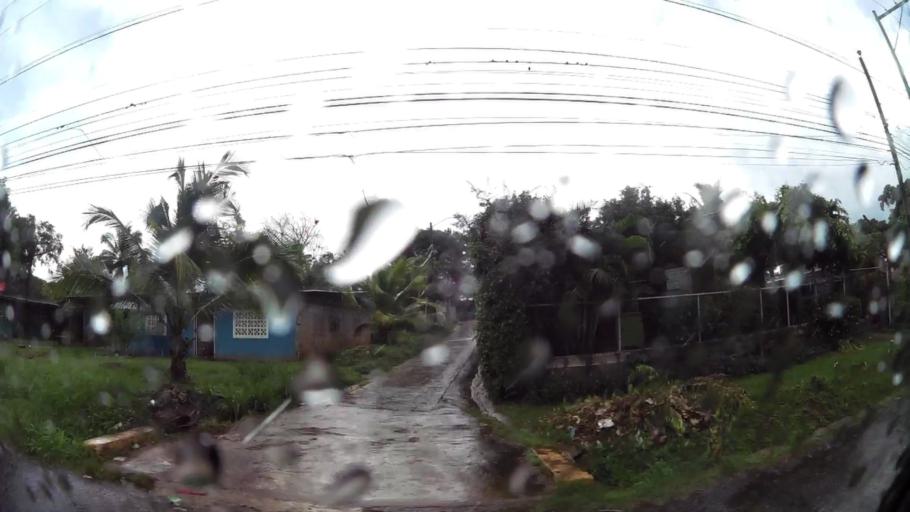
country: PA
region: Panama
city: Cabra Numero Uno
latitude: 9.1078
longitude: -79.3370
